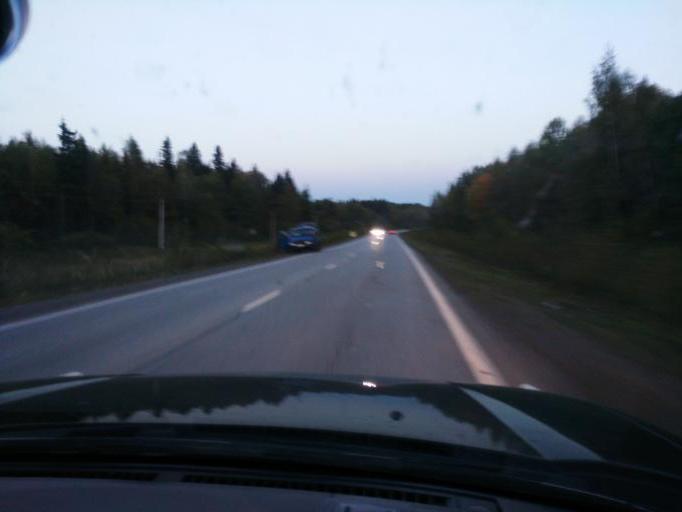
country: RU
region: Perm
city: Verkhnechusovskiye Gorodki
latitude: 58.2575
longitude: 56.9938
